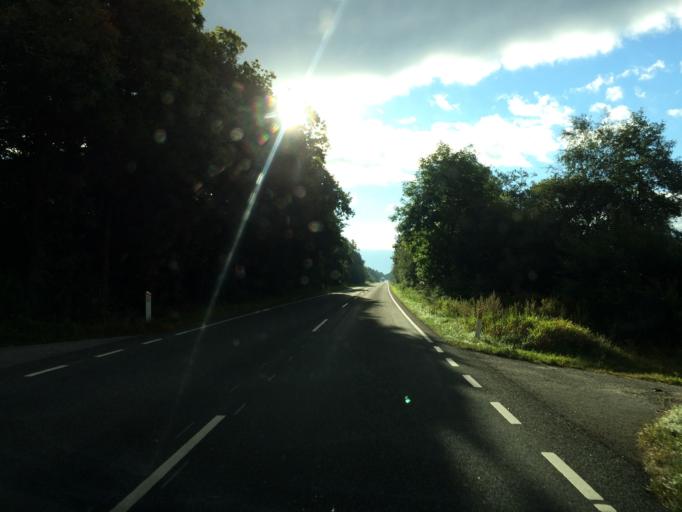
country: DK
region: Central Jutland
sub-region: Herning Kommune
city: Kibaek
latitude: 55.9552
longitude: 8.7228
